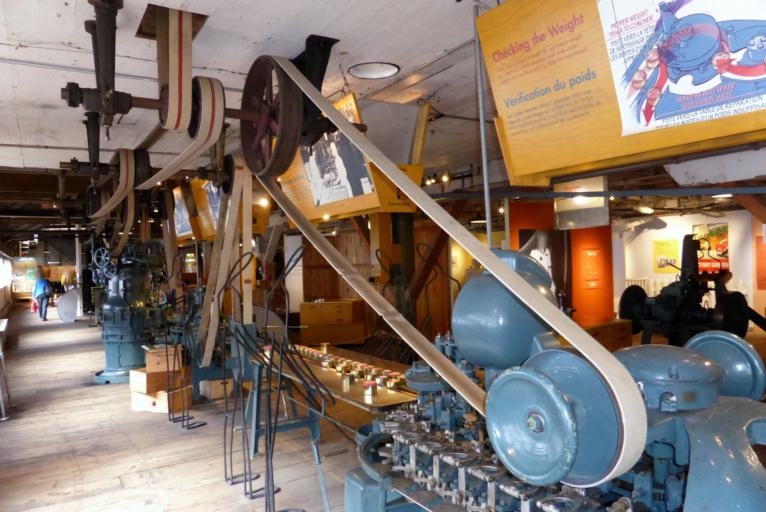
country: CA
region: British Columbia
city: Richmond
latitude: 49.1247
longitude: -123.1867
